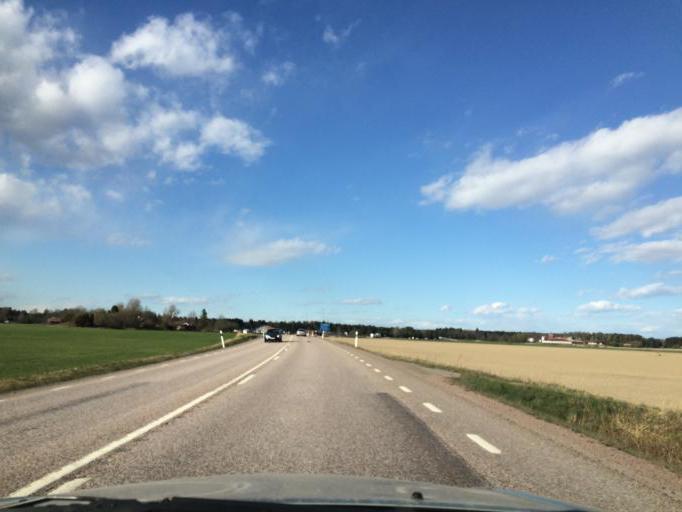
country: SE
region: Vaestmanland
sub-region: Hallstahammars Kommun
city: Kolback
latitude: 59.5531
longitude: 16.3376
